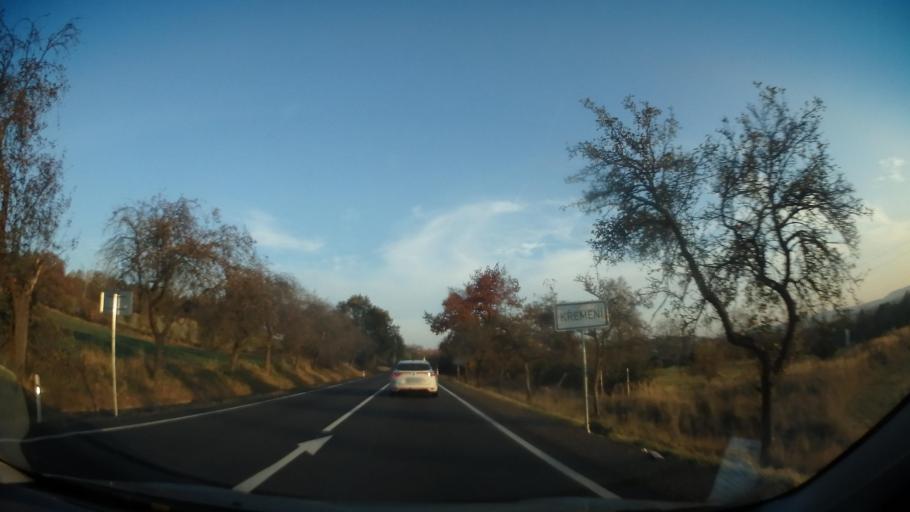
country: CZ
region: Central Bohemia
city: Postupice
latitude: 49.7474
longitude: 14.7908
